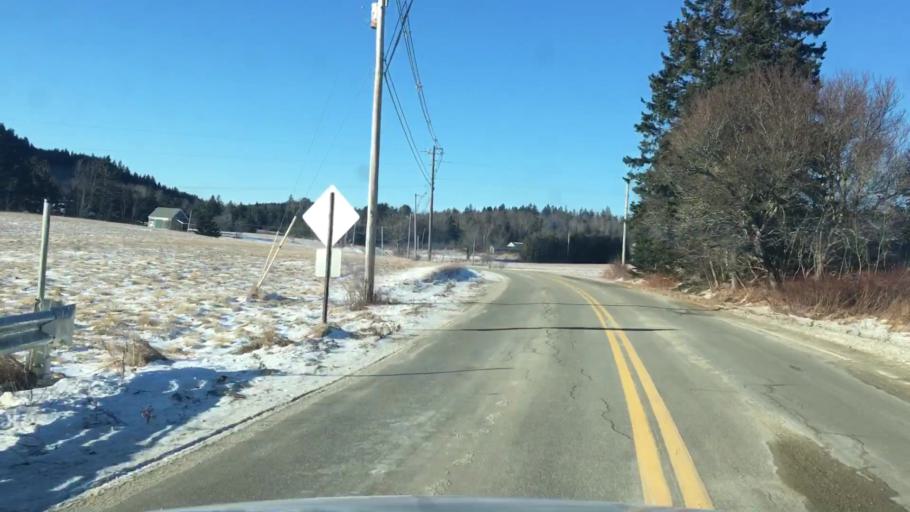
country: US
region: Maine
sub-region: Hancock County
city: Castine
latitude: 44.3501
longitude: -68.7490
